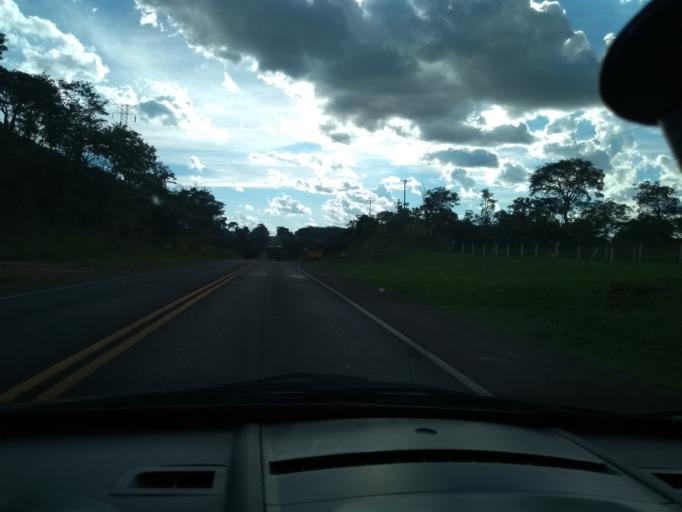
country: BR
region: Sao Paulo
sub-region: Casa Branca
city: Casa Branca
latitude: -21.7985
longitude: -47.0836
